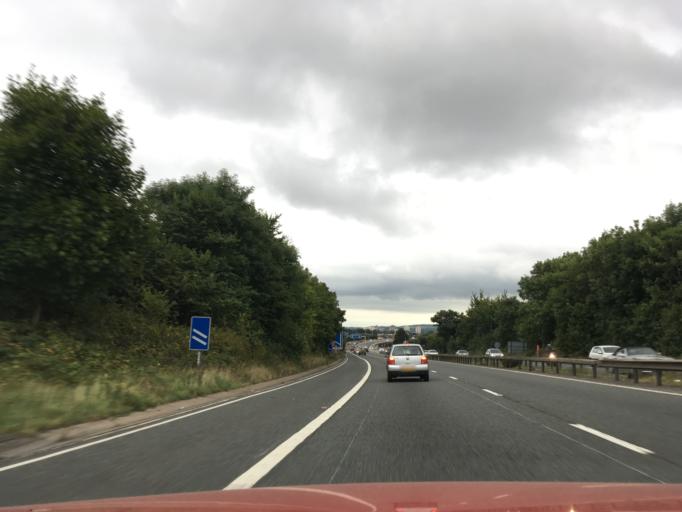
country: GB
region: England
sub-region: South Gloucestershire
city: Stoke Gifford
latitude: 51.4810
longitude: -2.5603
